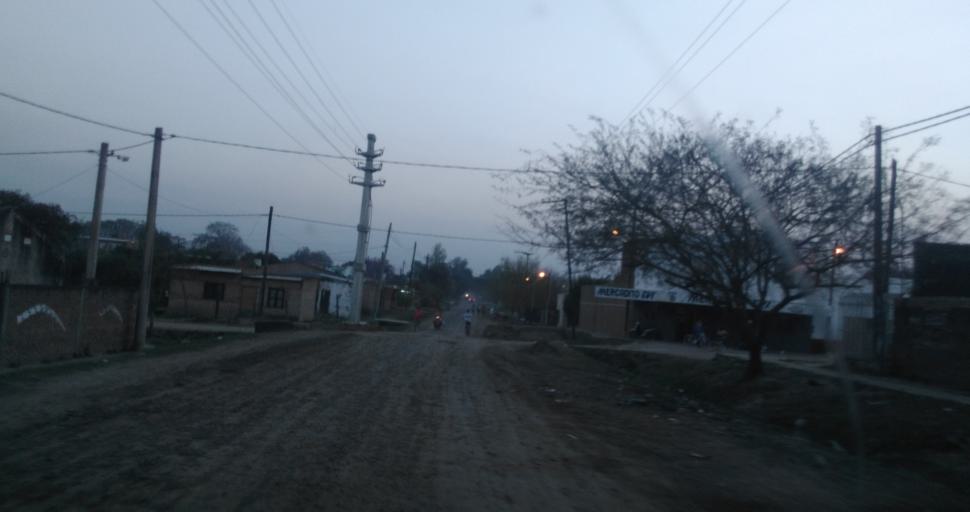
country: AR
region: Chaco
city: Fontana
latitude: -27.4279
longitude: -58.9944
